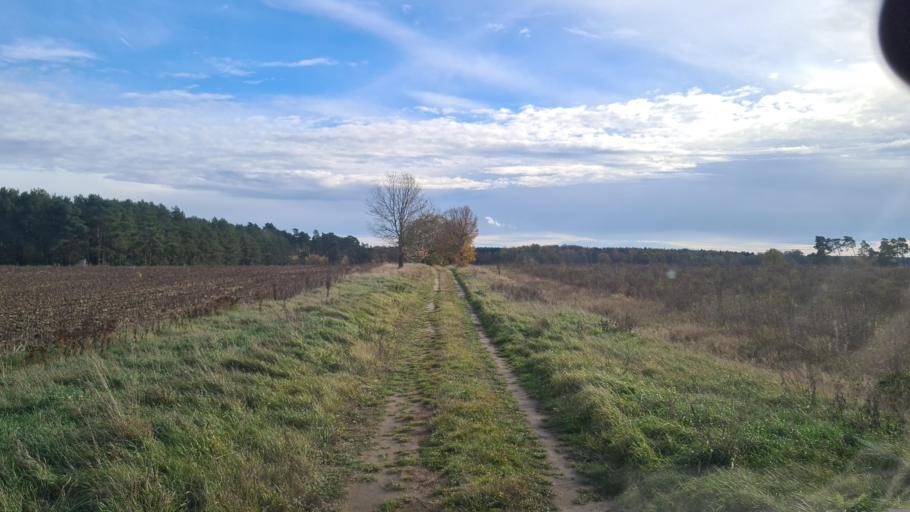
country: DE
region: Brandenburg
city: Wiesenburg
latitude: 52.0835
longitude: 12.4571
